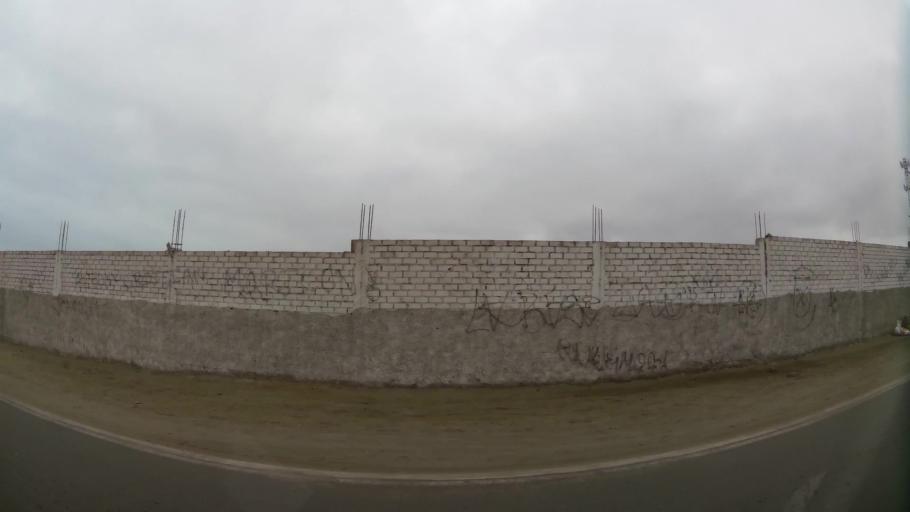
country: PE
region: Lima
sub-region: Lima
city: Punta Hermosa
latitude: -12.3349
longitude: -76.8221
